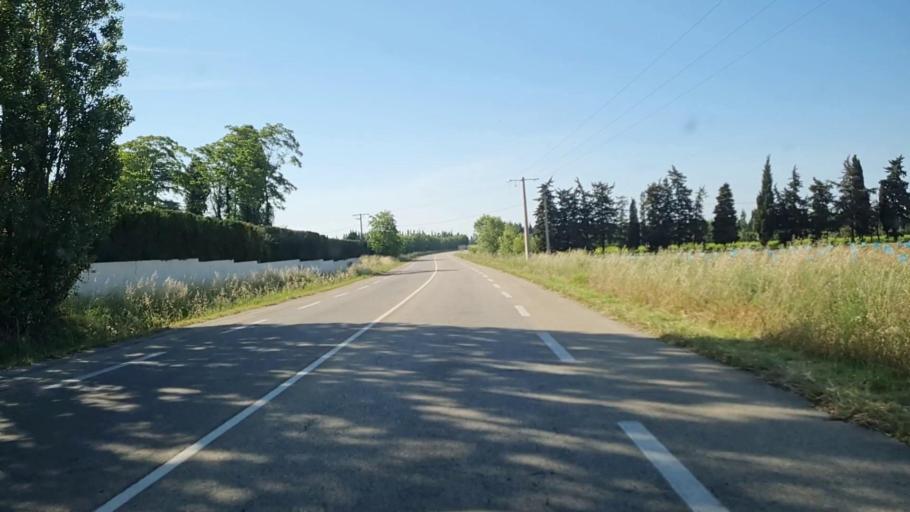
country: FR
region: Languedoc-Roussillon
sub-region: Departement du Gard
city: Garons
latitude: 43.7279
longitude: 4.4125
